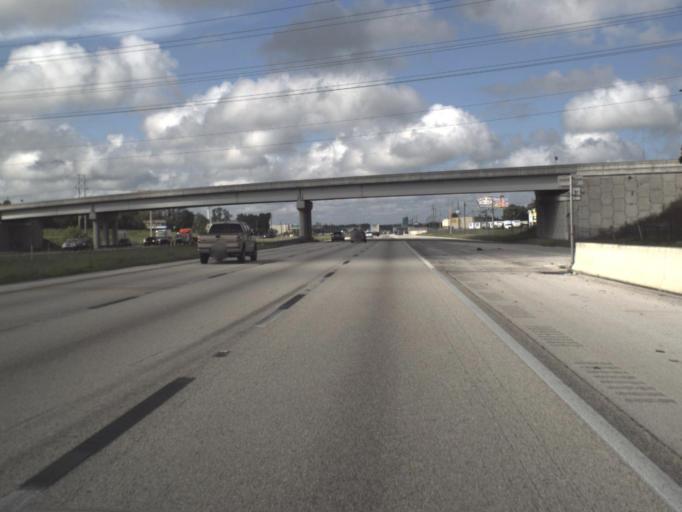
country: US
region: Florida
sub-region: Polk County
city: Winston
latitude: 28.0501
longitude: -82.0180
